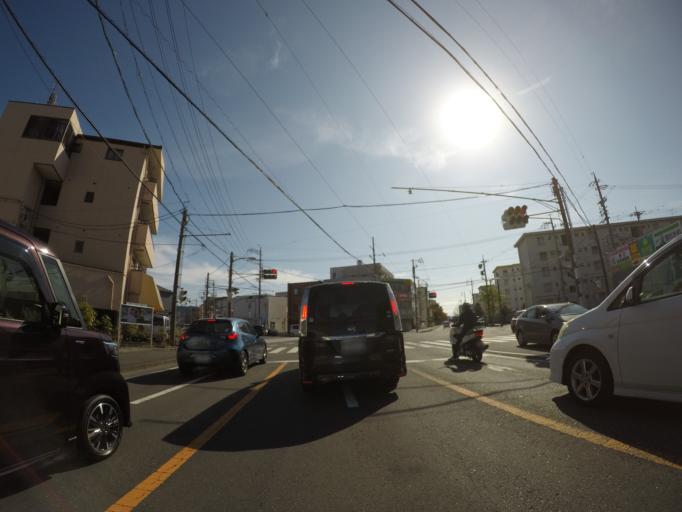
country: JP
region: Shizuoka
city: Shizuoka-shi
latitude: 34.9758
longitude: 138.4147
